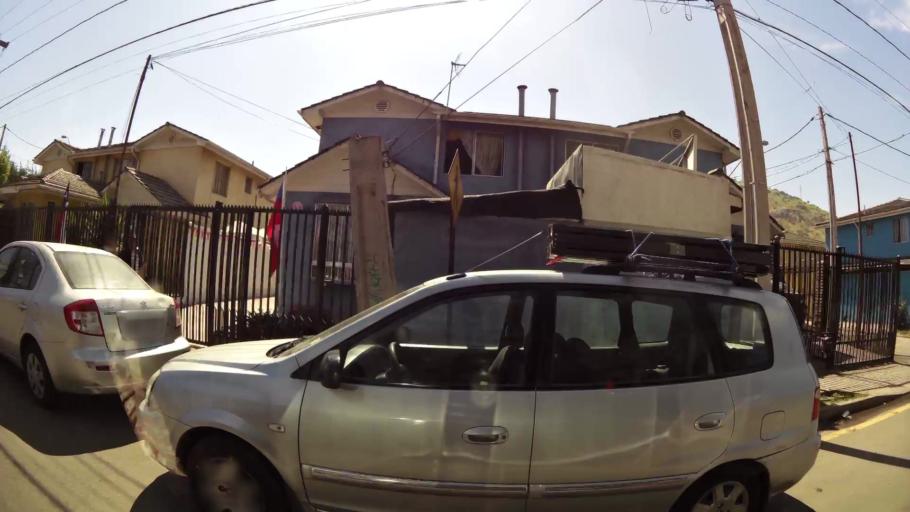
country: CL
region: Santiago Metropolitan
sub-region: Provincia de Santiago
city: Lo Prado
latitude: -33.3971
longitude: -70.7448
